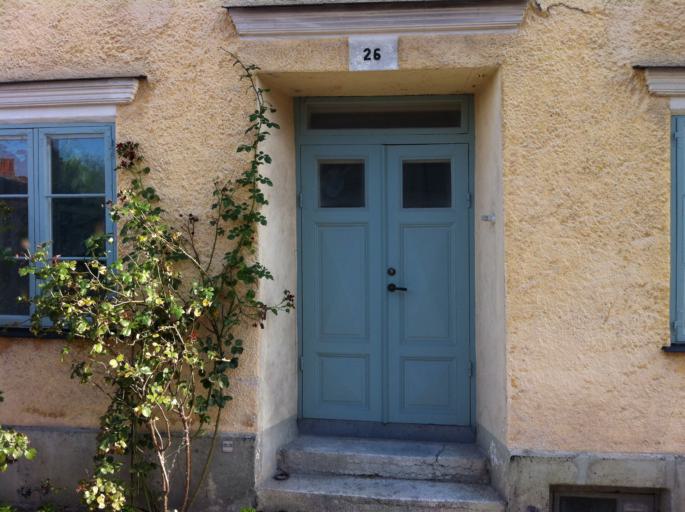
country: SE
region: Gotland
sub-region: Gotland
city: Visby
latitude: 57.6439
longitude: 18.2996
